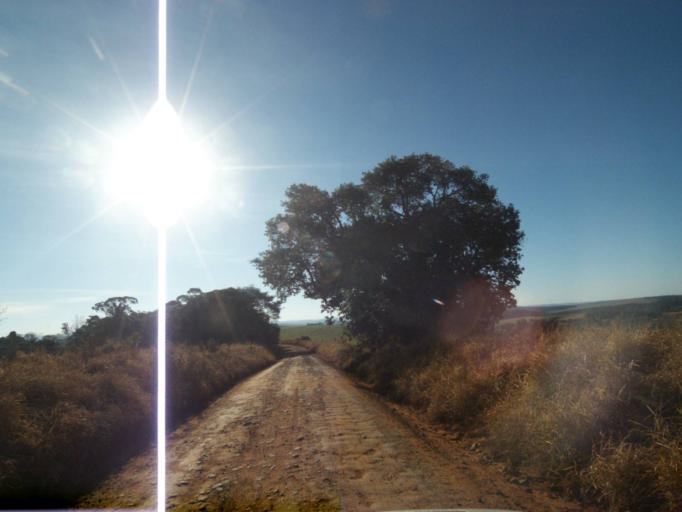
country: BR
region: Parana
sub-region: Telemaco Borba
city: Telemaco Borba
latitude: -24.5341
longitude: -50.6282
